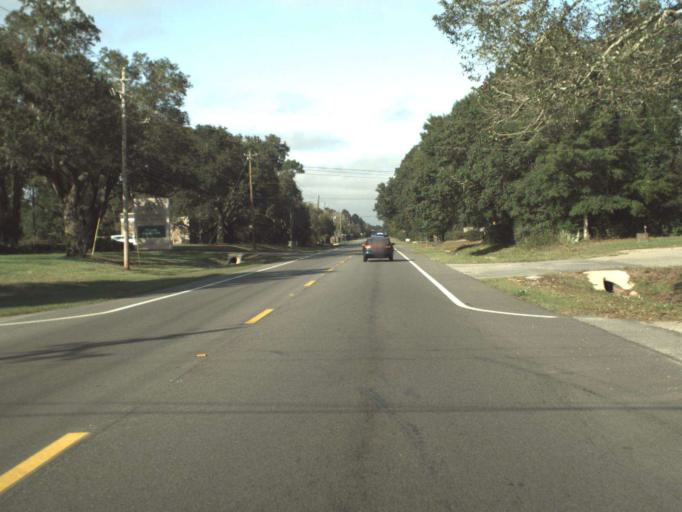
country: US
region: Florida
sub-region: Escambia County
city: Myrtle Grove
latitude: 30.4065
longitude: -87.3177
